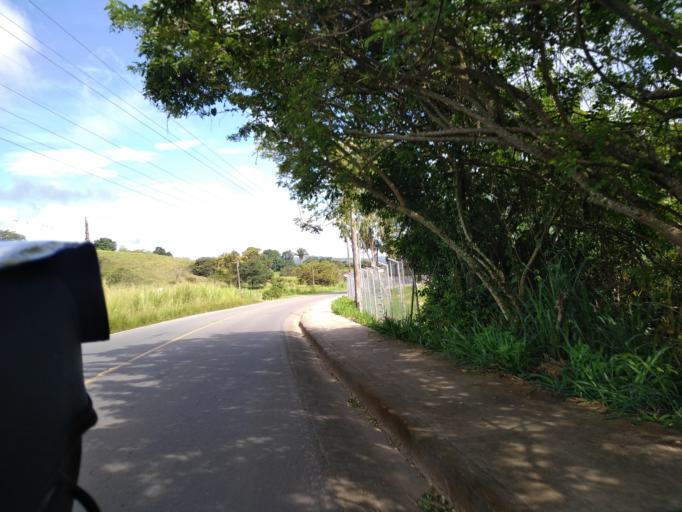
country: CO
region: Valle del Cauca
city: Caicedonia
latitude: 4.3407
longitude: -75.8455
